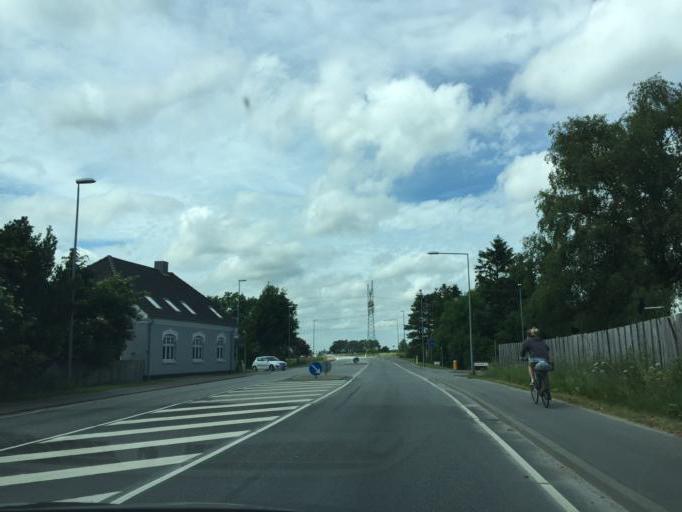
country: DK
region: South Denmark
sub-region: Odense Kommune
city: Hojby
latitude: 55.3312
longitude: 10.3930
